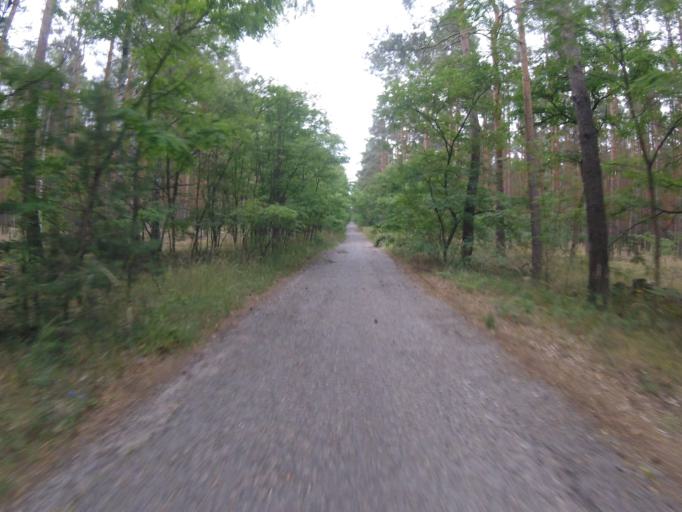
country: DE
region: Brandenburg
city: Gross Koris
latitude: 52.2118
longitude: 13.6900
